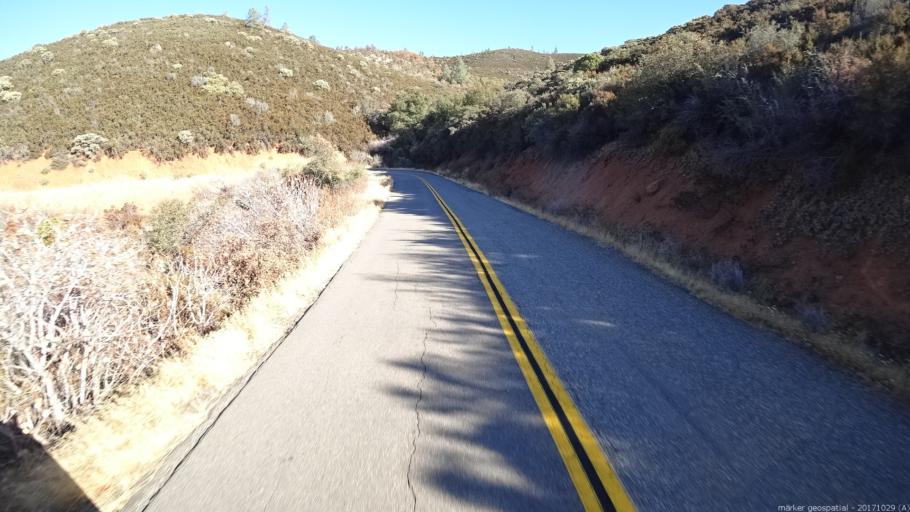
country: US
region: California
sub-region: Trinity County
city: Lewiston
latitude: 40.3656
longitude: -122.8683
